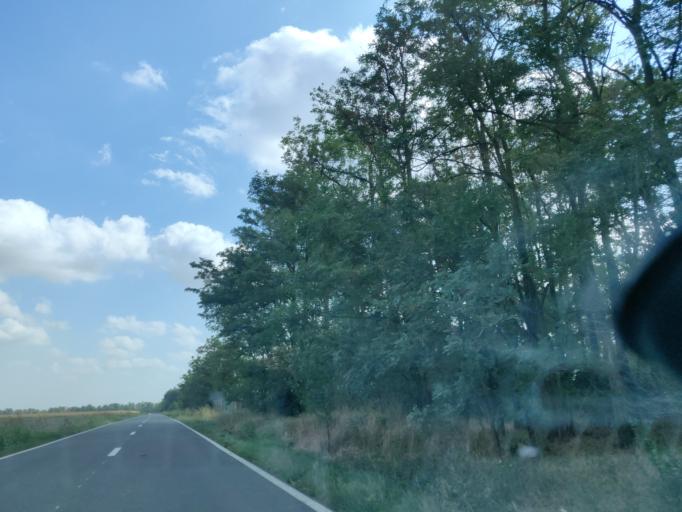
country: RO
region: Vrancea
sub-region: Comuna Maicanesti
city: Ramniceni
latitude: 45.4525
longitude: 27.3927
